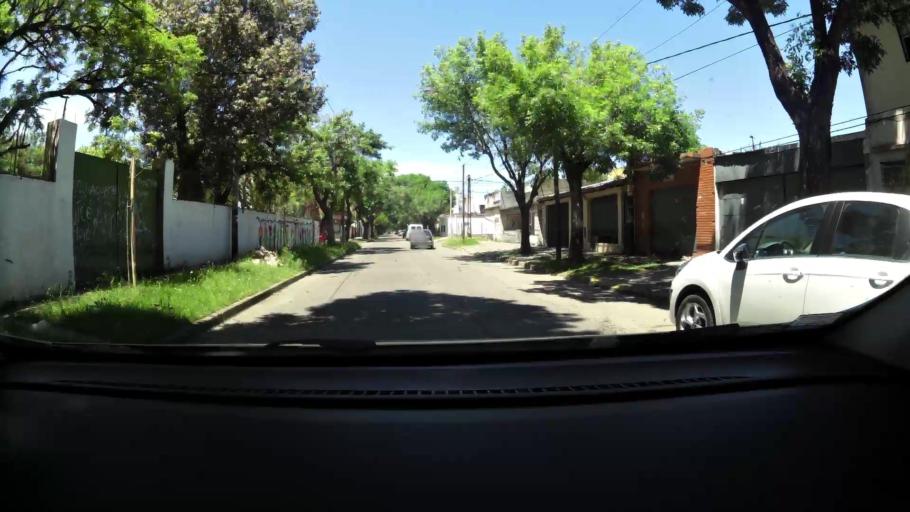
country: AR
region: Santa Fe
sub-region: Departamento de Rosario
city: Rosario
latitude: -32.9428
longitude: -60.7022
